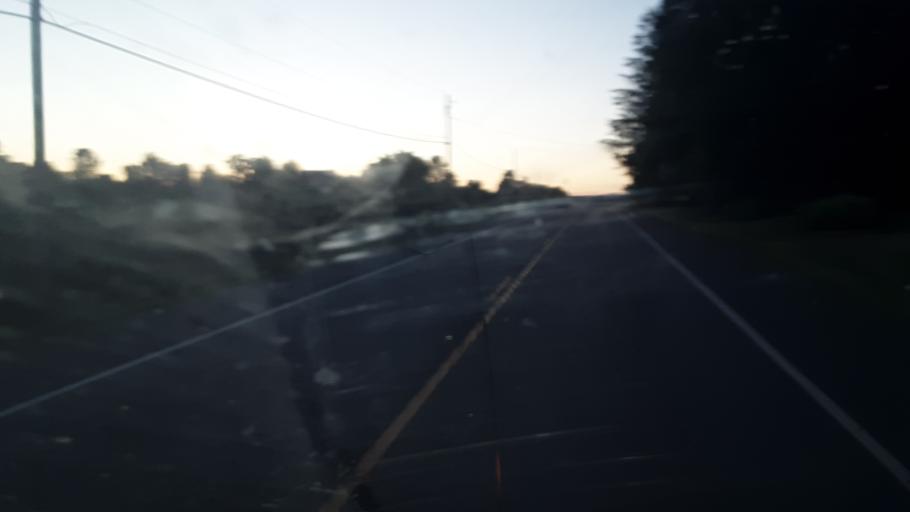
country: US
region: New York
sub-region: Montgomery County
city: Hagaman
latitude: 42.9685
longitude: -74.0967
